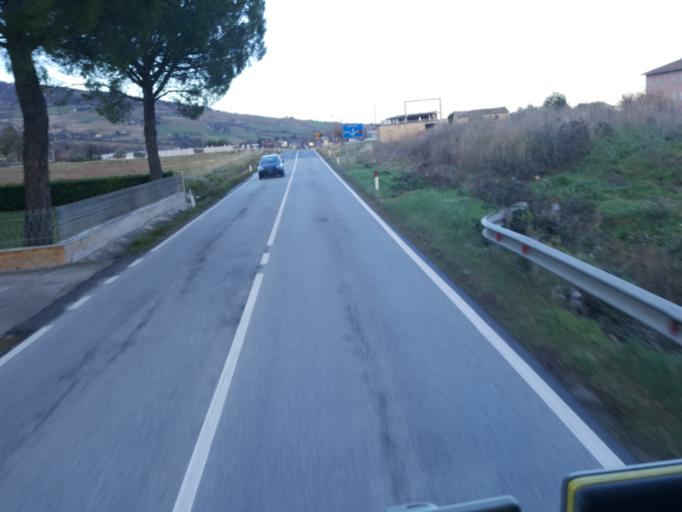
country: IT
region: The Marches
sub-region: Provincia di Macerata
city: San Severino Marche
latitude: 43.2472
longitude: 13.2260
